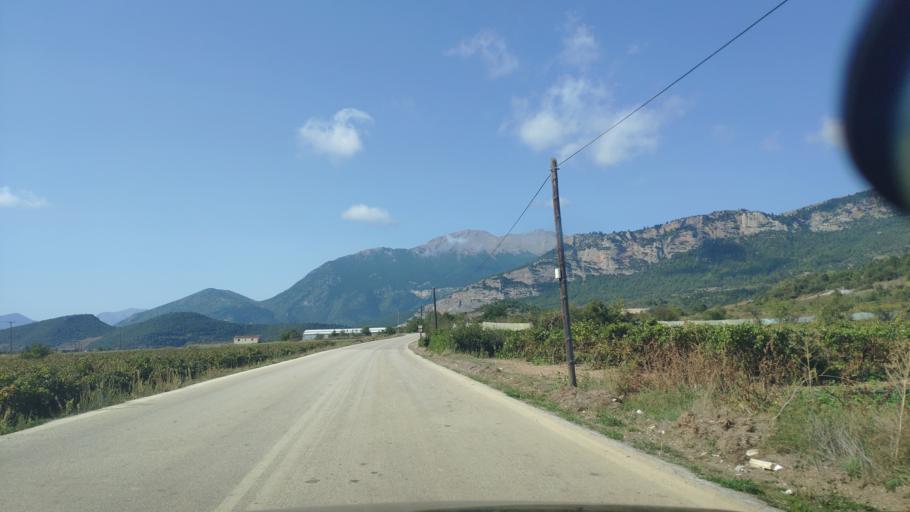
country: GR
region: Peloponnese
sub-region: Nomos Korinthias
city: Xylokastro
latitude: 37.9444
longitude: 22.5677
